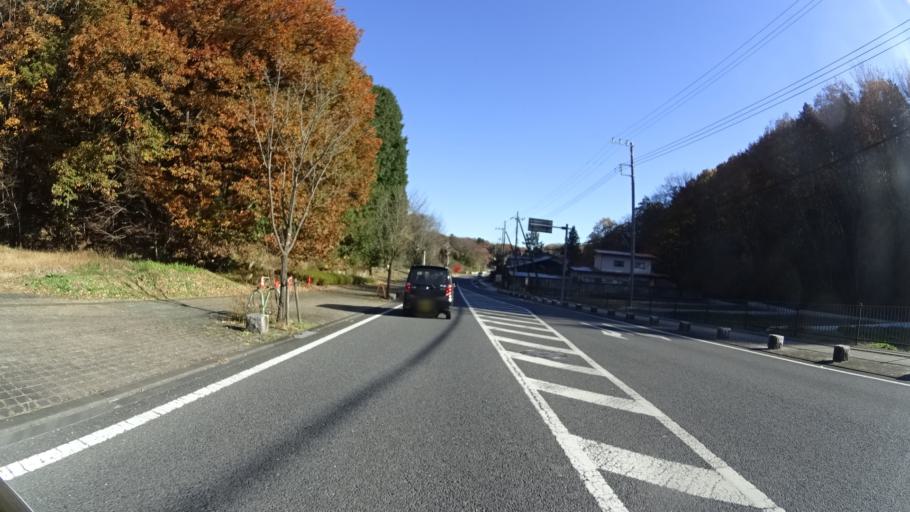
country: JP
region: Tochigi
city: Utsunomiya-shi
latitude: 36.6017
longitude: 139.8162
